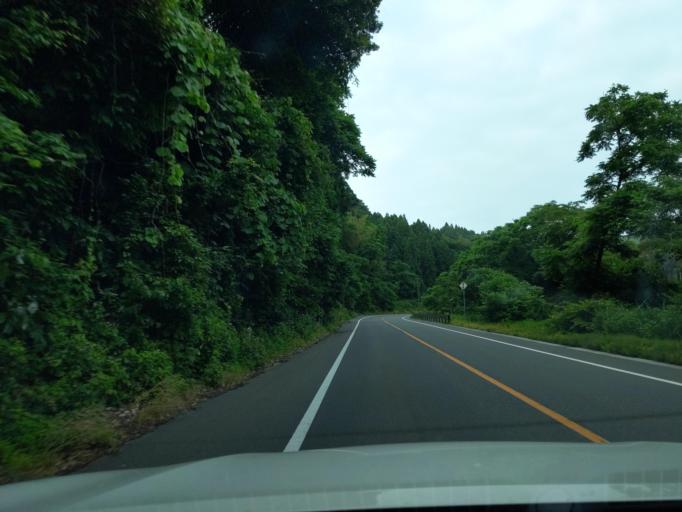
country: JP
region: Niigata
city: Kashiwazaki
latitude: 37.4465
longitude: 138.6794
